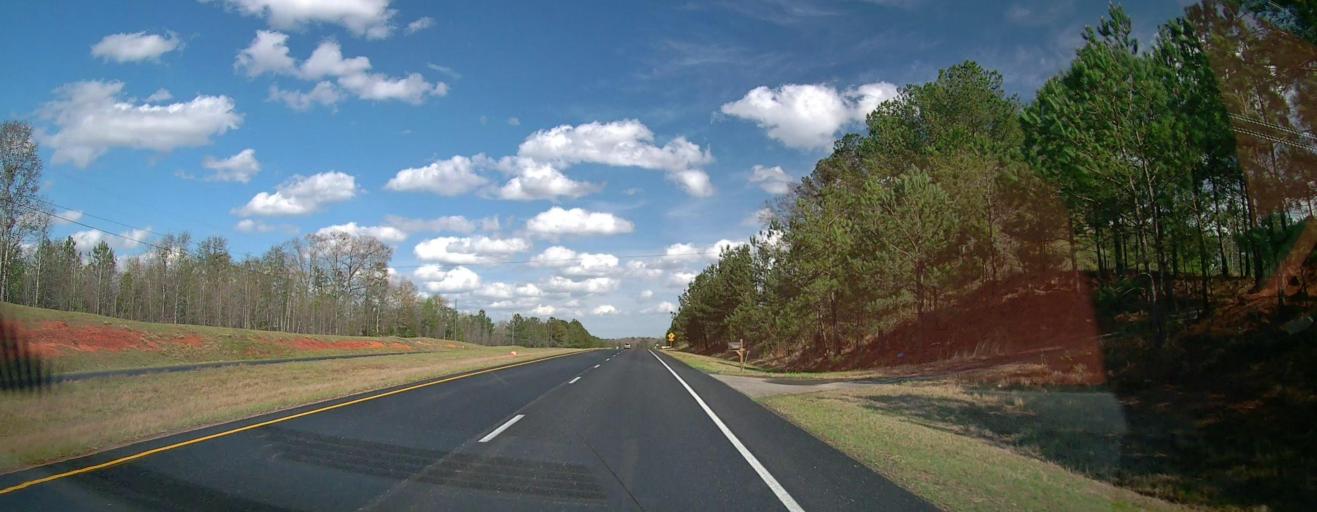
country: US
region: Georgia
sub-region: Wilkinson County
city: Gordon
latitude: 32.8482
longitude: -83.4365
